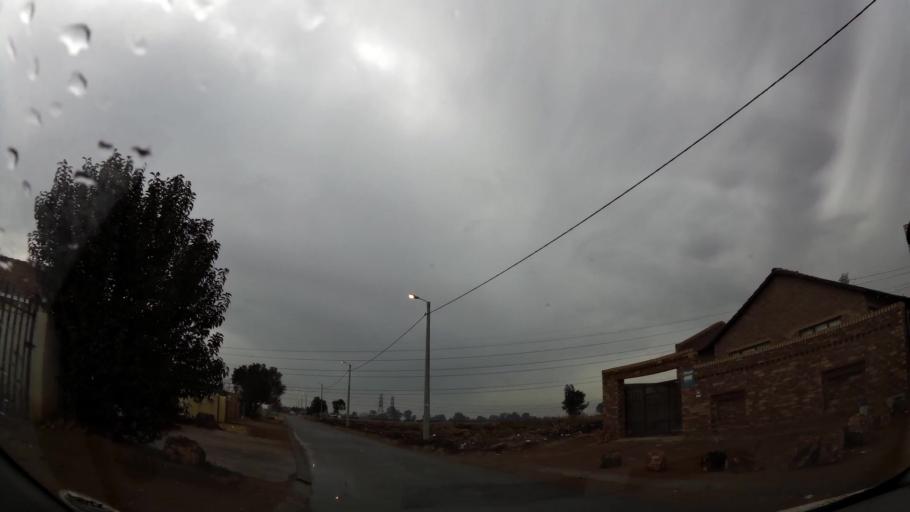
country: ZA
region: Gauteng
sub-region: Ekurhuleni Metropolitan Municipality
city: Germiston
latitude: -26.3401
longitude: 28.2117
